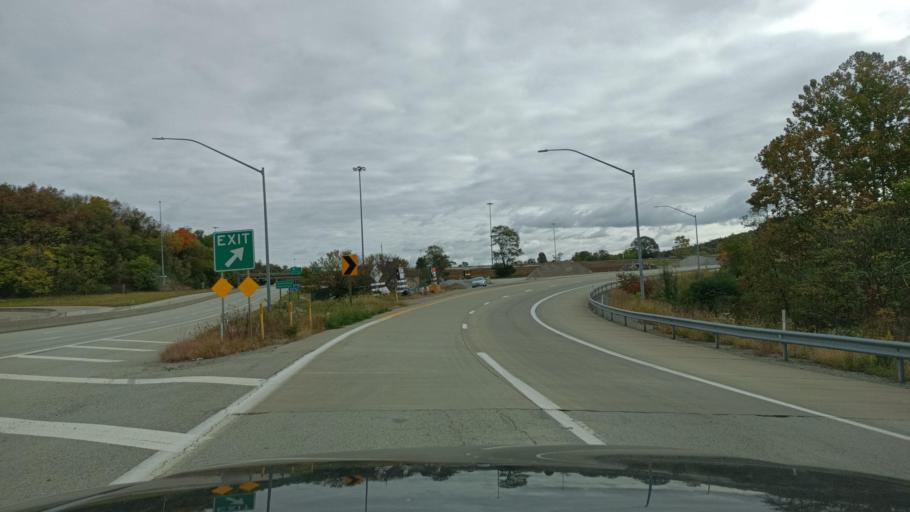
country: US
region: Pennsylvania
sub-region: Westmoreland County
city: New Stanton
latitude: 40.2232
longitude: -79.5971
